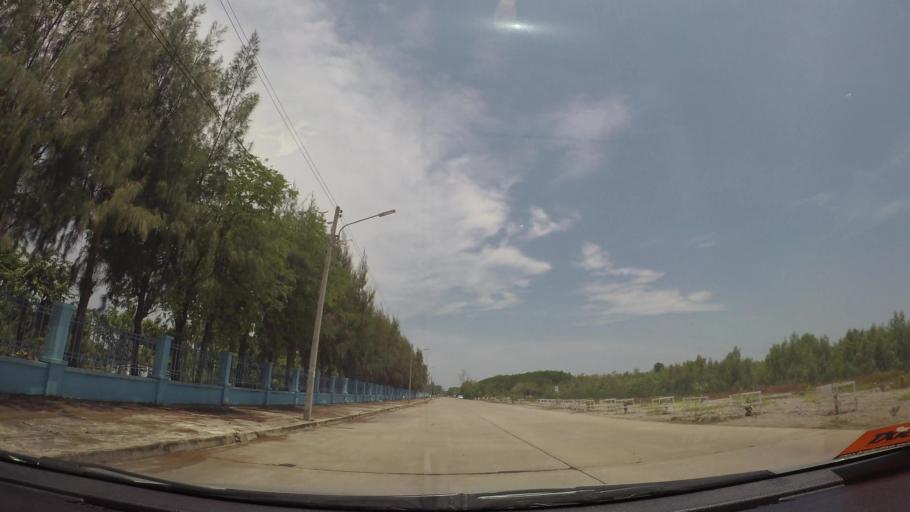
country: TH
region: Chon Buri
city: Chon Buri
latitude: 13.3437
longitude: 100.9479
